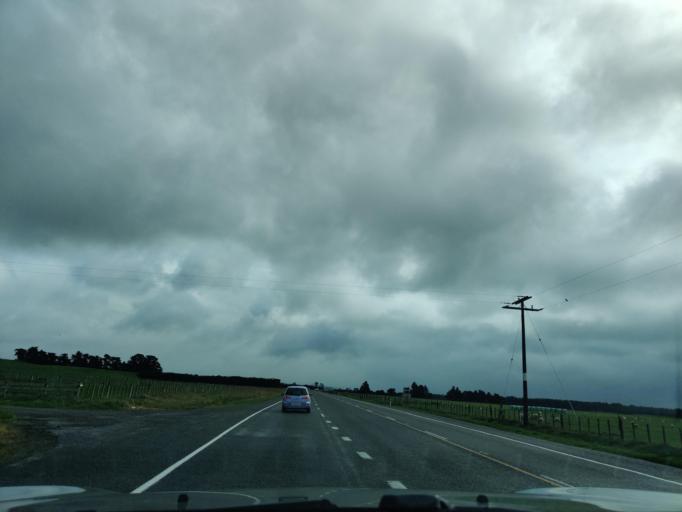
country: NZ
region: Hawke's Bay
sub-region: Hastings District
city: Hastings
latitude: -40.0208
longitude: 176.3110
